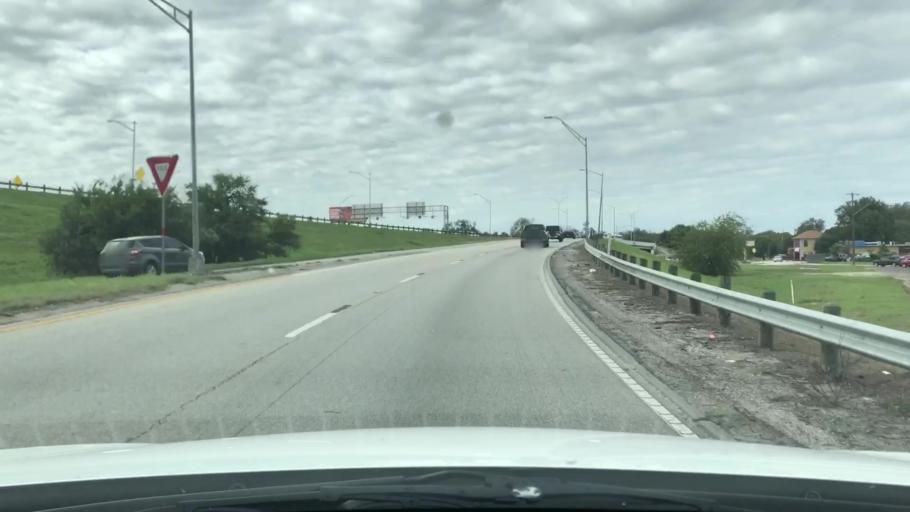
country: US
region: Texas
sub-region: Bexar County
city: San Antonio
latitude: 29.3969
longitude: -98.5131
